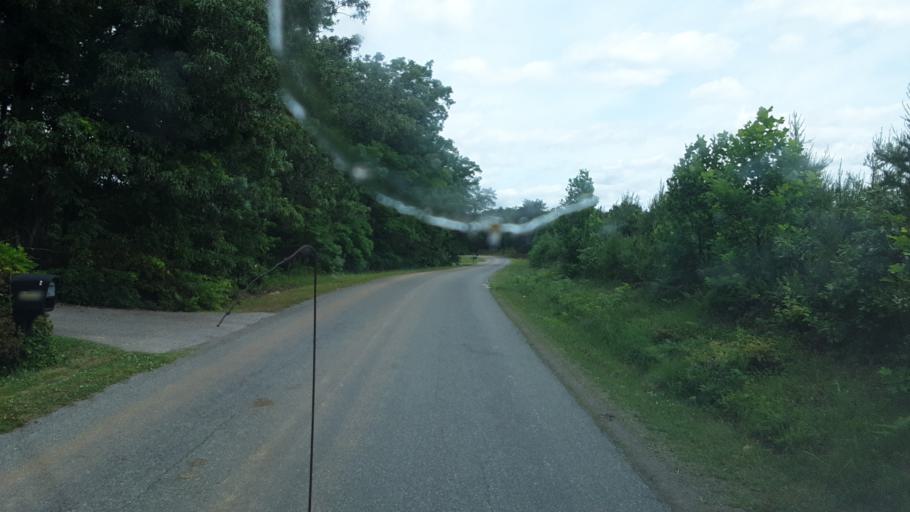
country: US
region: Virginia
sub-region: Pittsylvania County
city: Chatham
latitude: 36.8569
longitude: -79.4476
